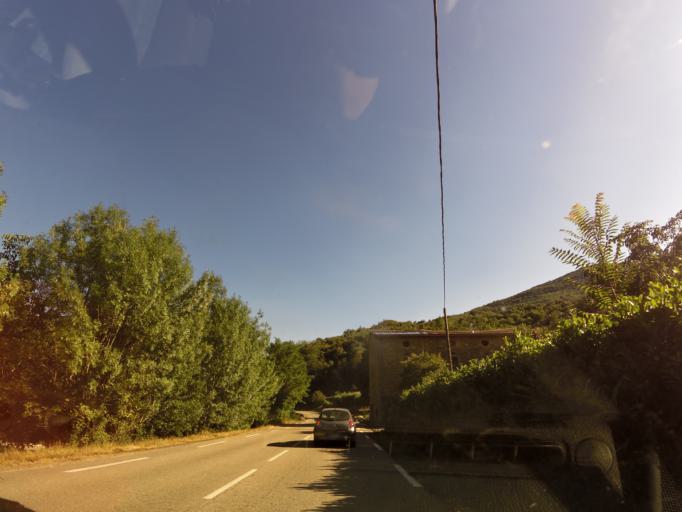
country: FR
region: Languedoc-Roussillon
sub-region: Departement du Gard
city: Valleraugue
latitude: 44.0398
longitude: 3.6720
